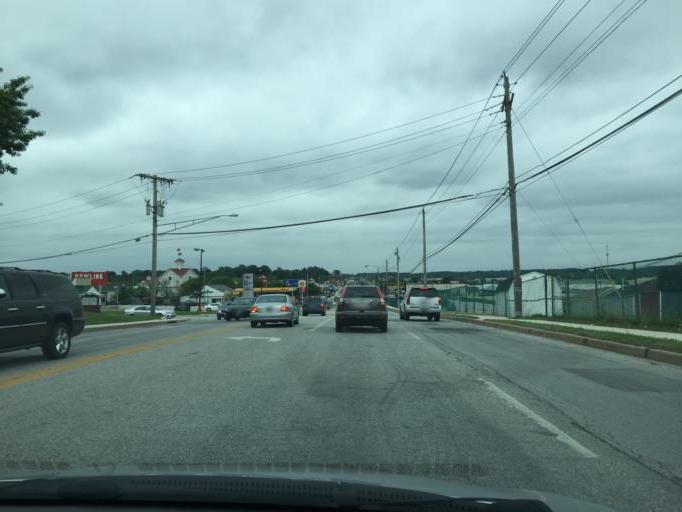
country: US
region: Maryland
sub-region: Baltimore County
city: Timonium
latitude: 39.4458
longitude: -76.6286
